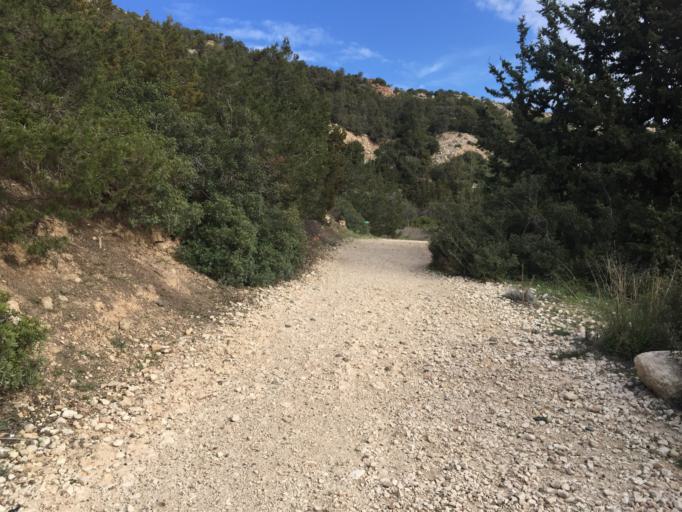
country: CY
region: Pafos
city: Pegeia
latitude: 34.9216
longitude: 32.3385
